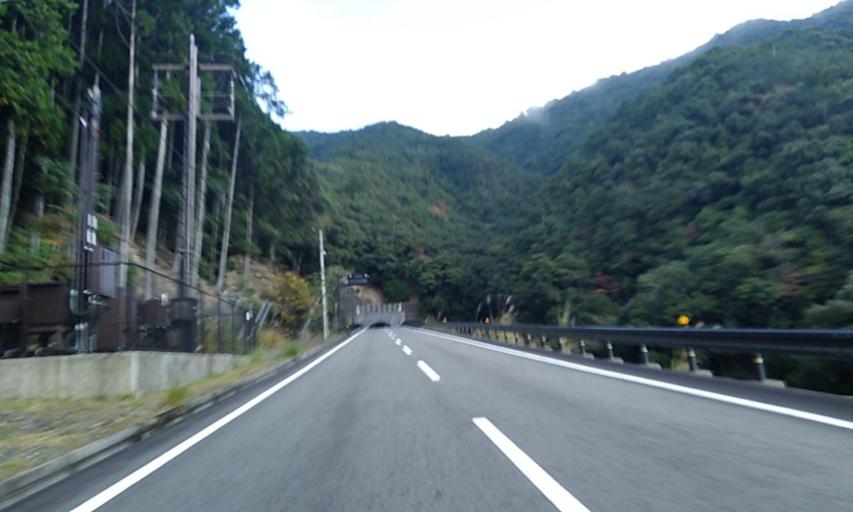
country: JP
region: Wakayama
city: Shingu
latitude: 33.8791
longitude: 135.8765
